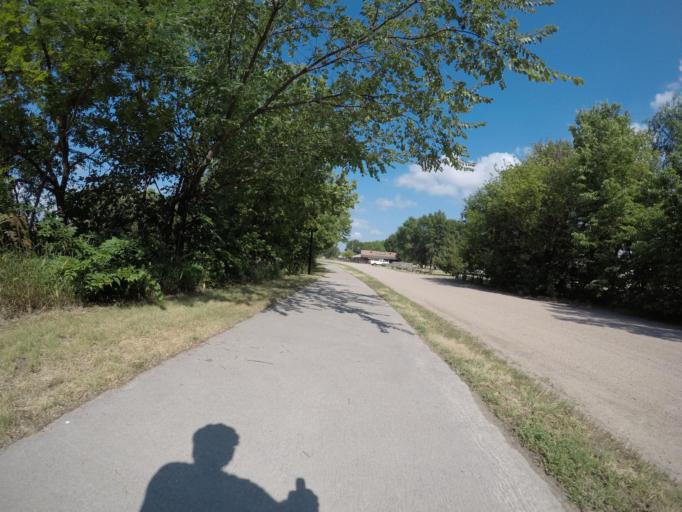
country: US
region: Nebraska
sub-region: Buffalo County
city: Kearney
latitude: 40.6741
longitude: -99.0651
